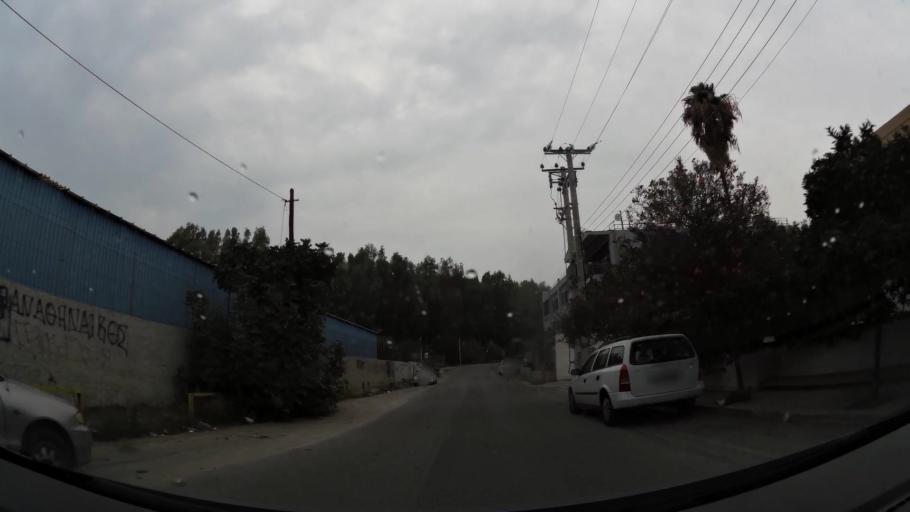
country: GR
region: Attica
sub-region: Nomarchia Athinas
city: Argyroupoli
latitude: 37.9168
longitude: 23.7402
